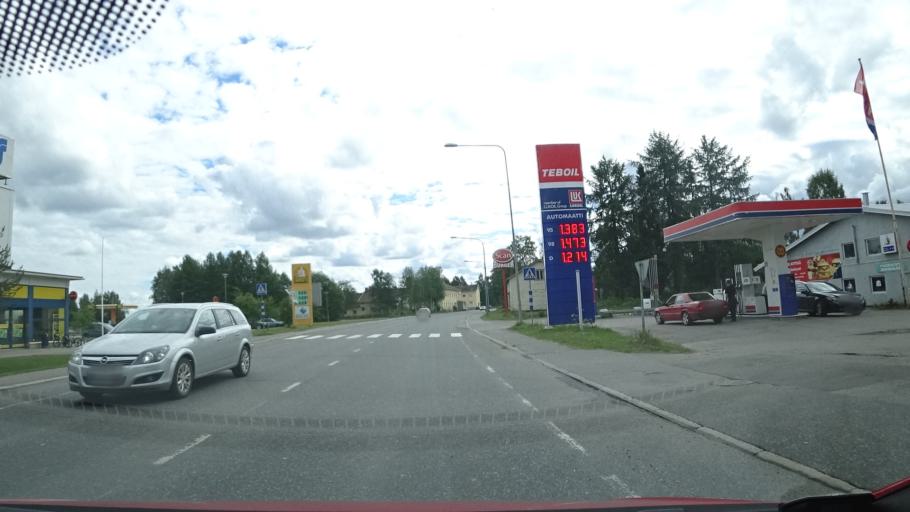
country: FI
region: Lapland
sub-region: Tunturi-Lappi
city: Kittilae
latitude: 67.6611
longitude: 24.9026
